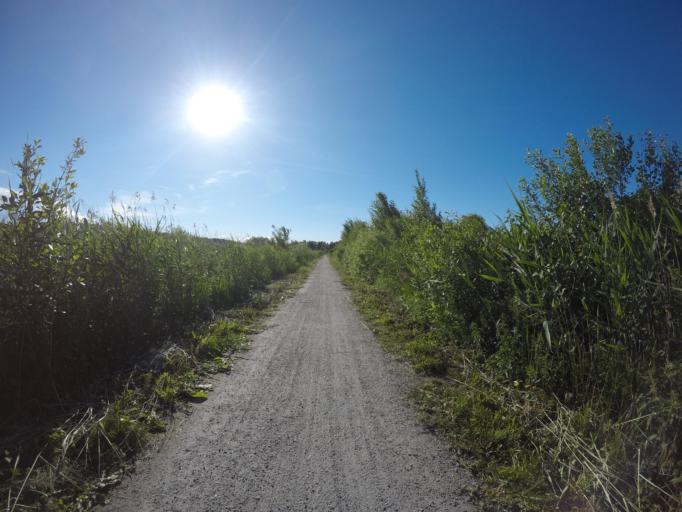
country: SE
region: Vaestmanland
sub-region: Vasteras
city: Vasteras
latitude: 59.5746
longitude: 16.6316
